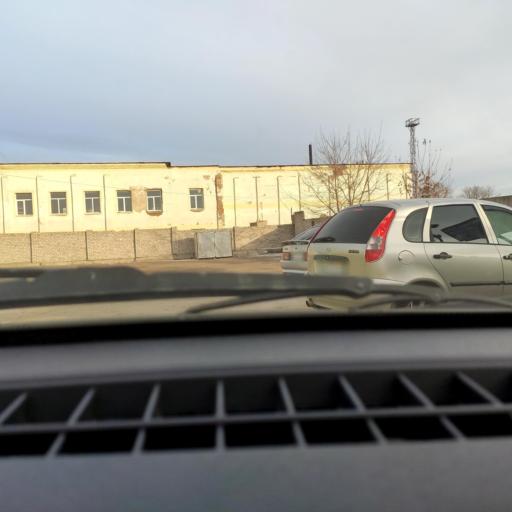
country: RU
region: Bashkortostan
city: Ufa
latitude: 54.7452
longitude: 55.9222
